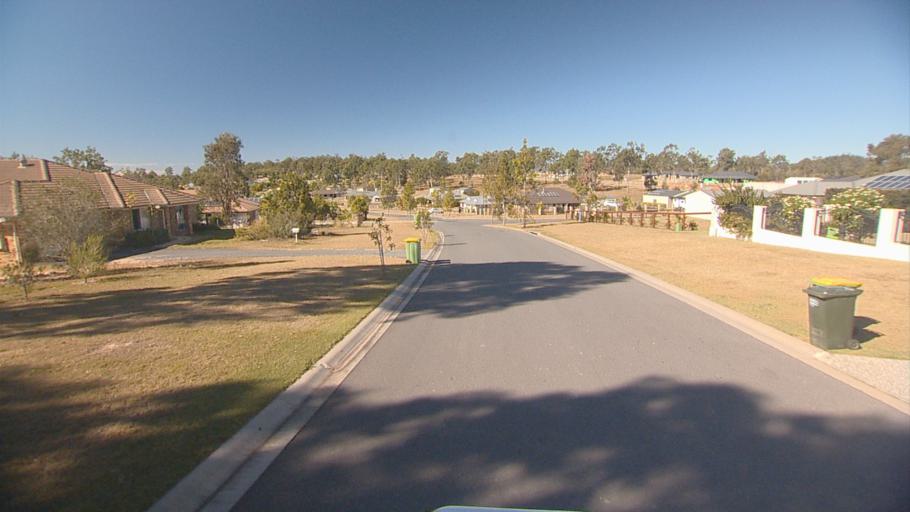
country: AU
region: Queensland
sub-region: Logan
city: North Maclean
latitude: -27.7573
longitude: 152.9452
